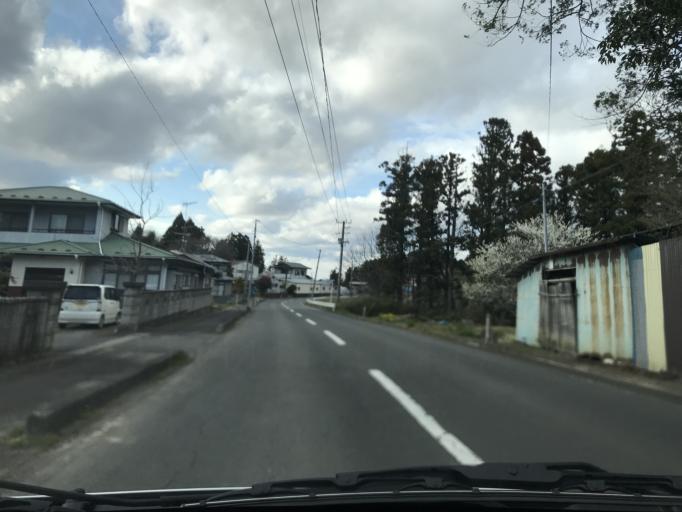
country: JP
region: Miyagi
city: Wakuya
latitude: 38.6385
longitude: 141.2137
